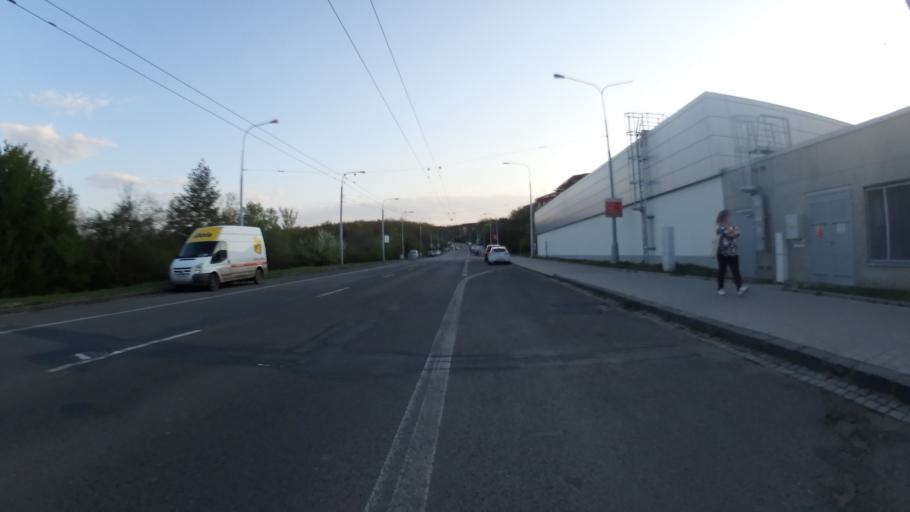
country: CZ
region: South Moravian
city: Troubsko
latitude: 49.1958
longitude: 16.5333
